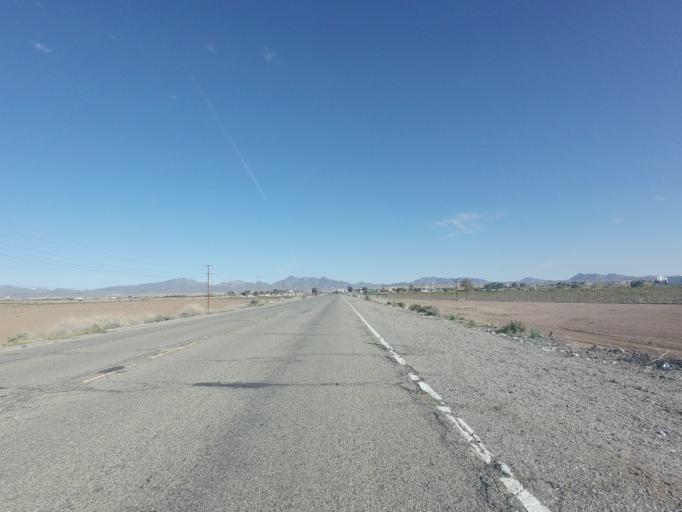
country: US
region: Arizona
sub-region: La Paz County
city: Ehrenberg
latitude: 33.6091
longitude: -114.5462
